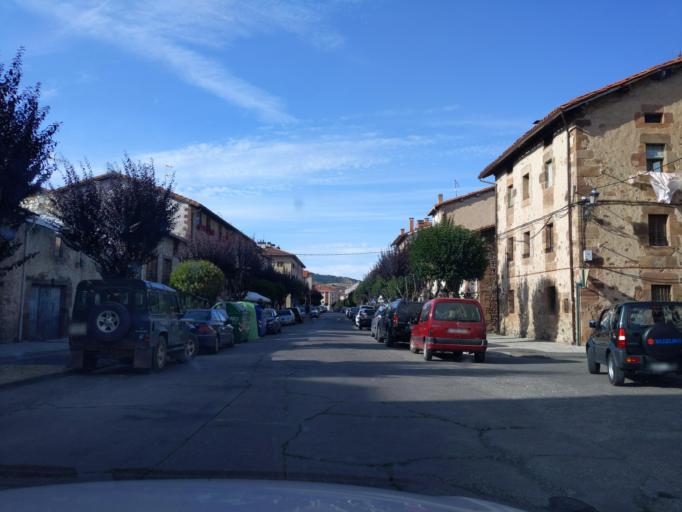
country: ES
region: La Rioja
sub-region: Provincia de La Rioja
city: Ezcaray
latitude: 42.3250
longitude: -3.0122
